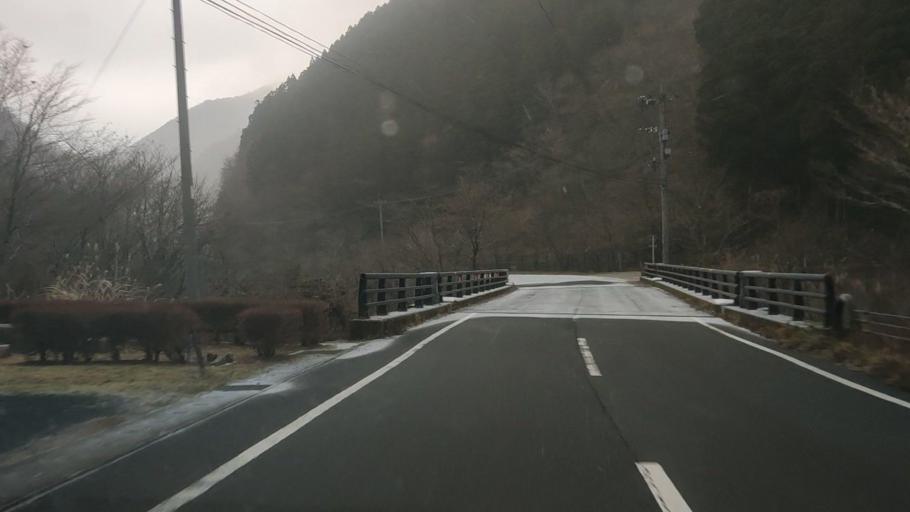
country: JP
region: Kumamoto
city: Matsubase
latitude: 32.5602
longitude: 130.9171
